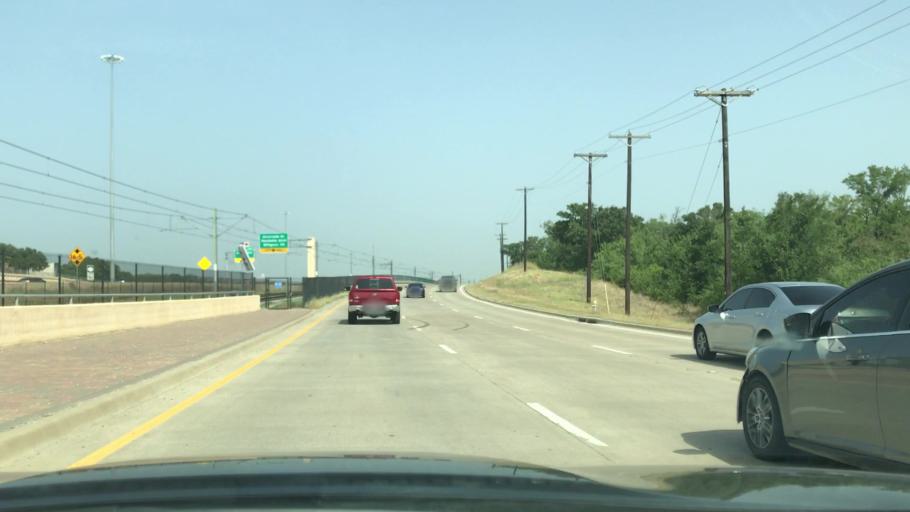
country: US
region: Texas
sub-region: Dallas County
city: Irving
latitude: 32.8509
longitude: -96.9185
